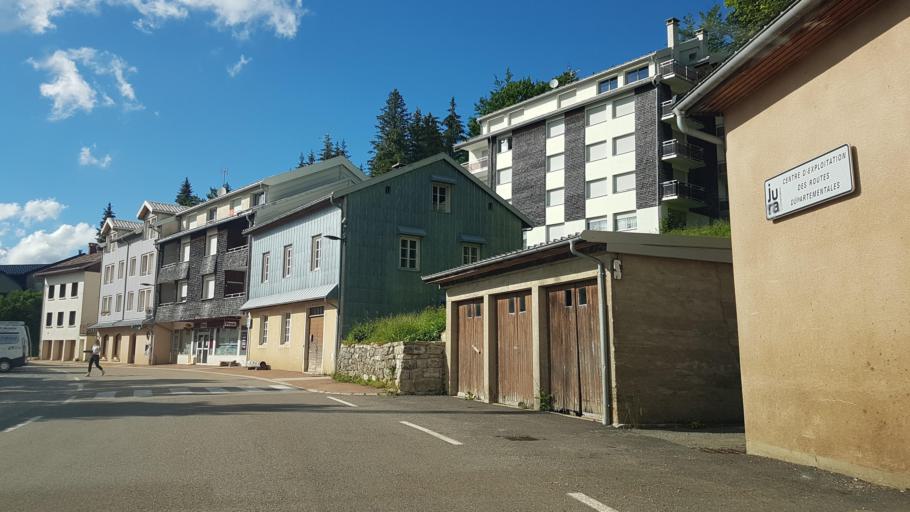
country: FR
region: Franche-Comte
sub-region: Departement du Jura
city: Longchaumois
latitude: 46.3942
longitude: 5.9681
